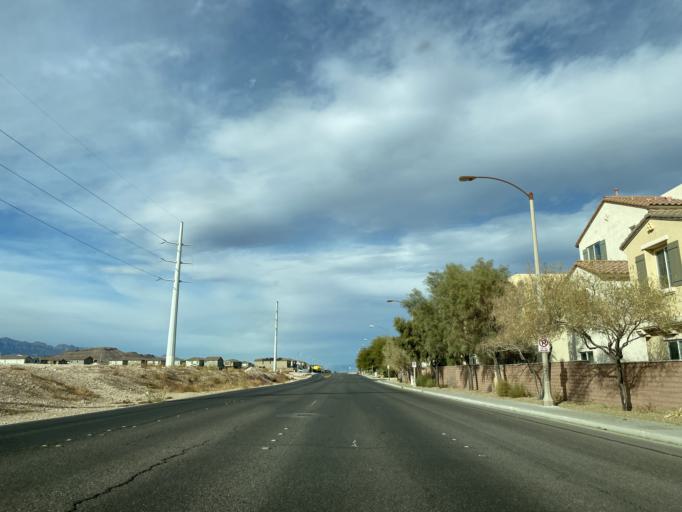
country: US
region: Nevada
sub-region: Clark County
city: Enterprise
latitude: 36.0094
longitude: -115.2982
